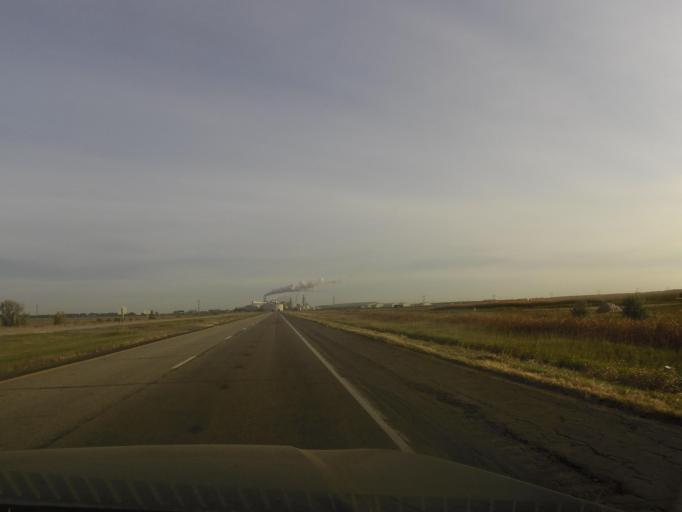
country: US
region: North Dakota
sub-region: Walsh County
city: Grafton
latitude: 48.5792
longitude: -97.1841
